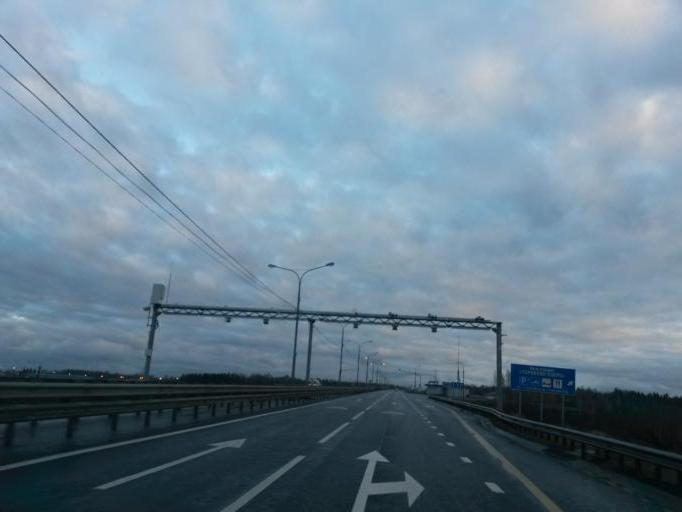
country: RU
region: Moskovskaya
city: Svatkovo
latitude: 56.3334
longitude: 38.2583
